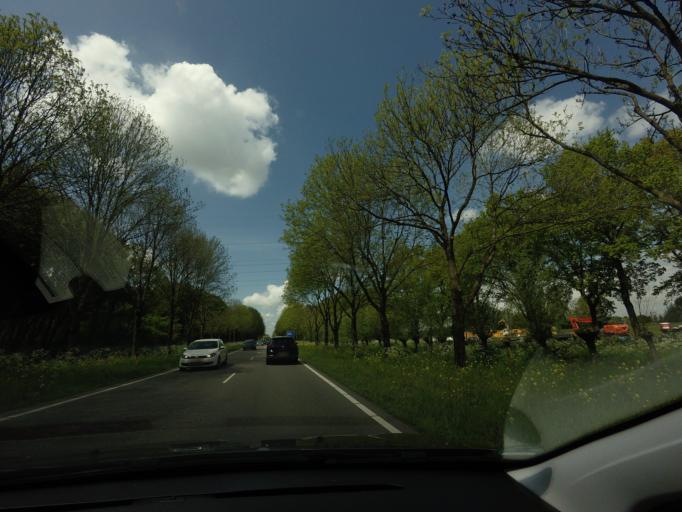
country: NL
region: Utrecht
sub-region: Gemeente Nieuwegein
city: Nieuwegein
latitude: 52.0696
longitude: 5.0591
